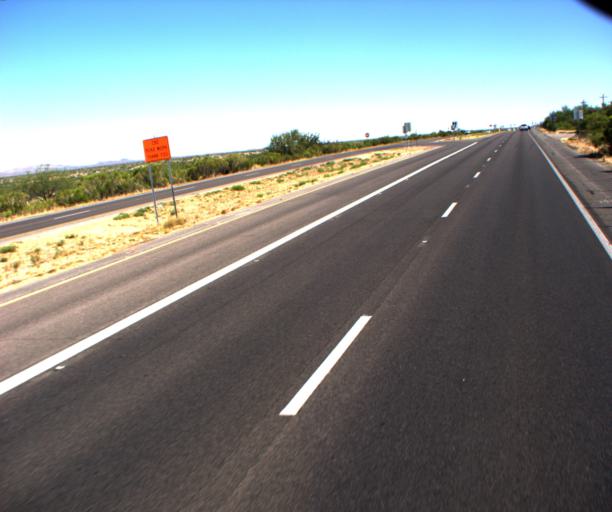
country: US
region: Arizona
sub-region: Pima County
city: Catalina
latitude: 32.5178
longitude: -110.9266
